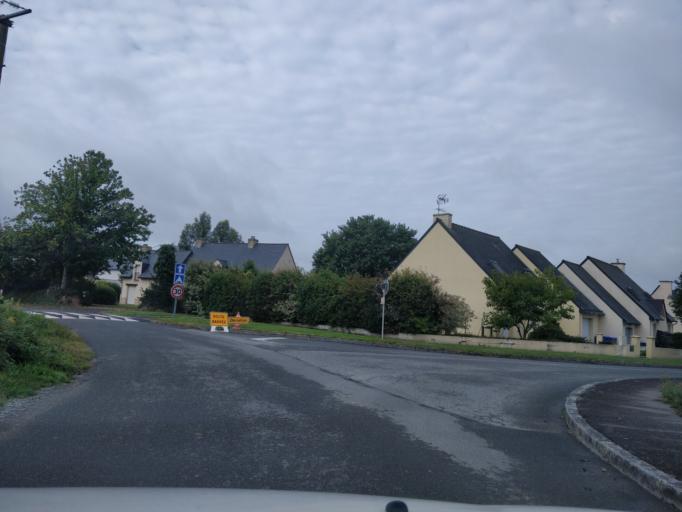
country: FR
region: Brittany
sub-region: Departement d'Ille-et-Vilaine
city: La Bouexiere
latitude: 48.1783
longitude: -1.4344
